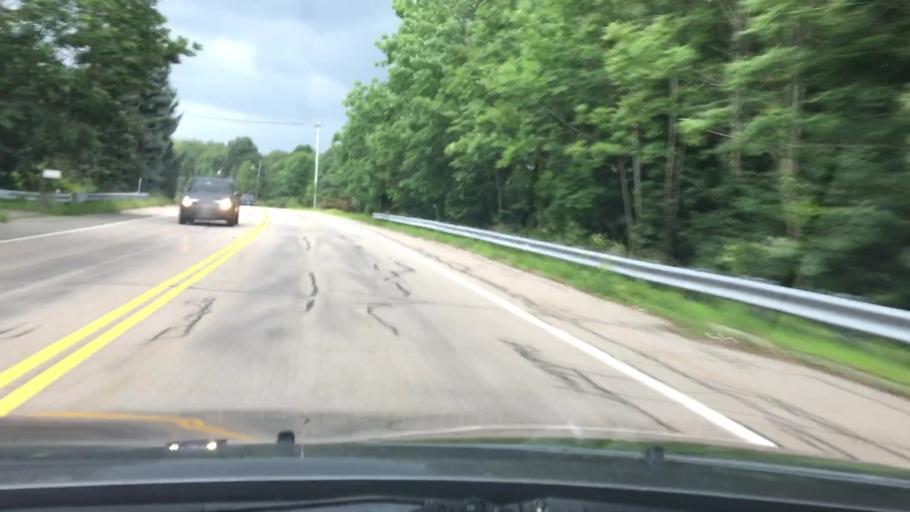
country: US
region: Massachusetts
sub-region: Norfolk County
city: Plainville
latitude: 41.9664
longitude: -71.3676
